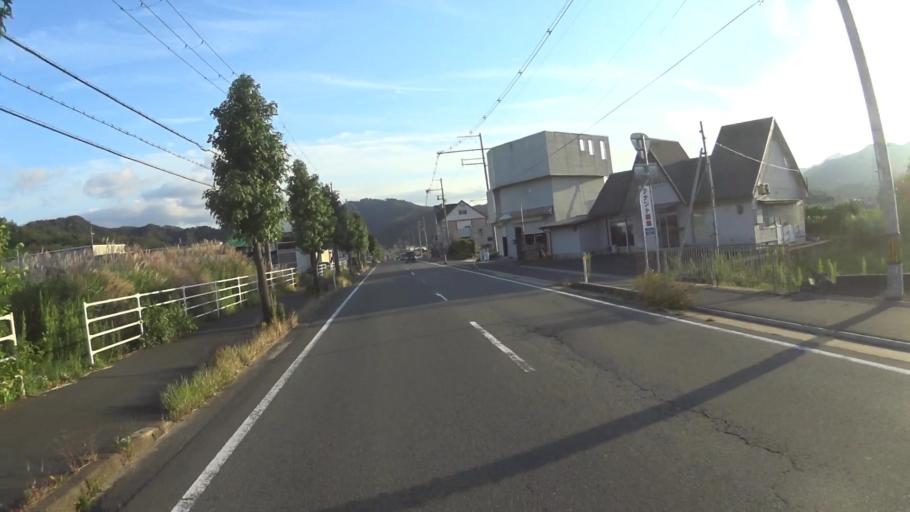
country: JP
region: Kyoto
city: Miyazu
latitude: 35.5775
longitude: 135.0990
